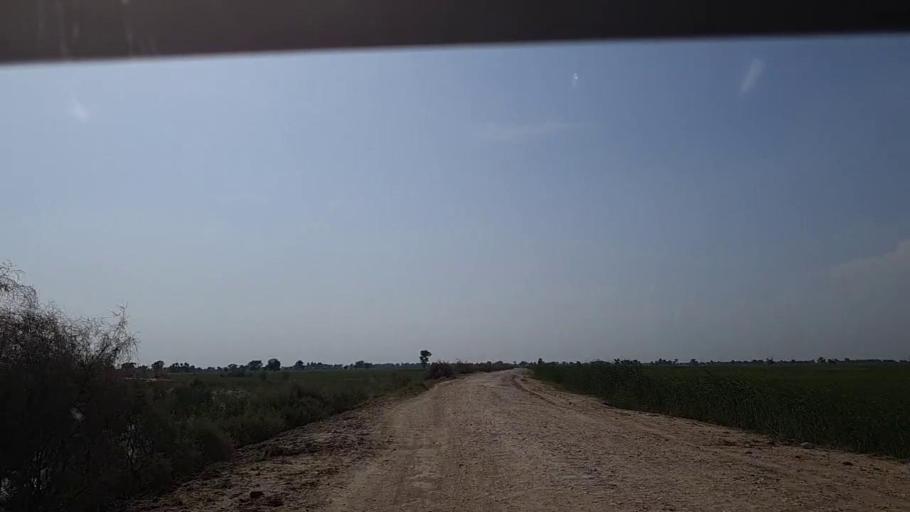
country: PK
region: Sindh
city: Khanpur
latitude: 27.8494
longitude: 69.3677
